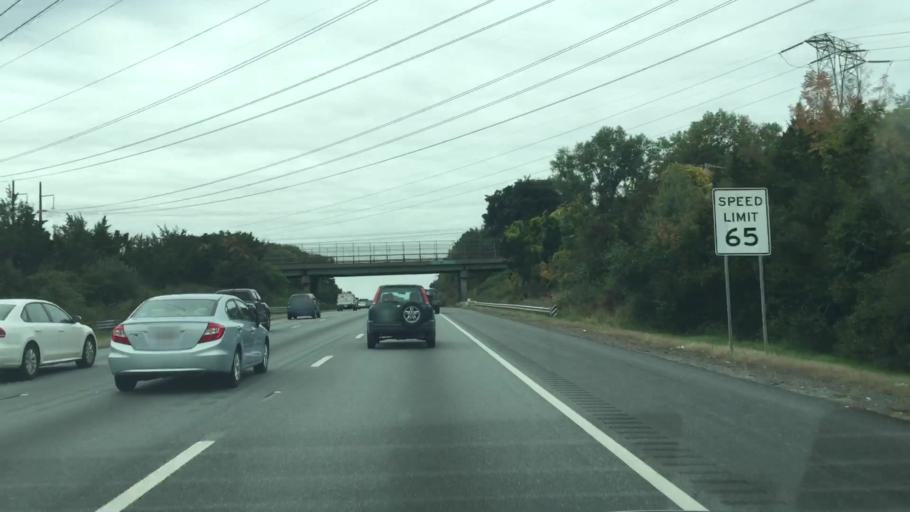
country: US
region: Massachusetts
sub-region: Middlesex County
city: Tewksbury
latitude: 42.6394
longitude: -71.2391
